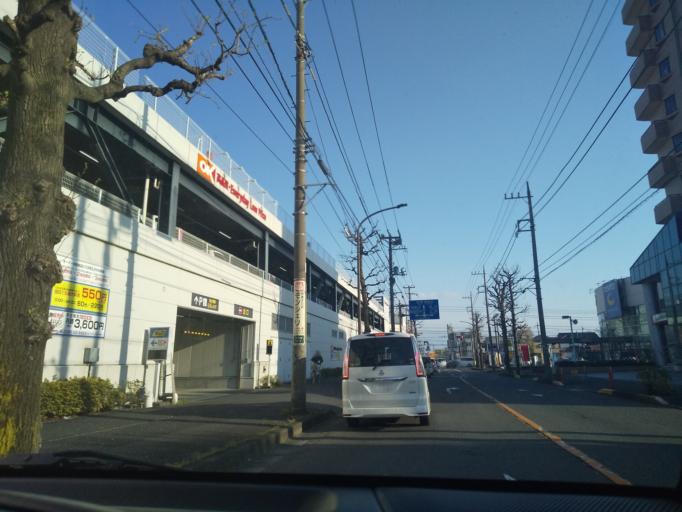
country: JP
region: Kanagawa
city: Zama
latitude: 35.5592
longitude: 139.3746
